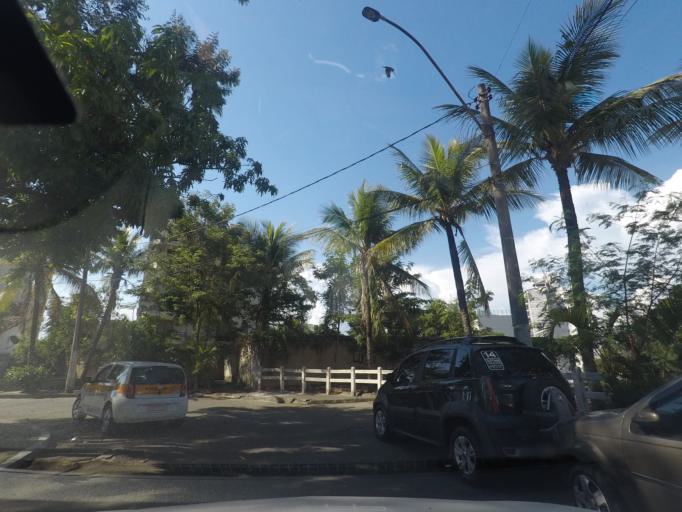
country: BR
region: Rio de Janeiro
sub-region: Niteroi
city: Niteroi
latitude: -22.9065
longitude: -43.1307
